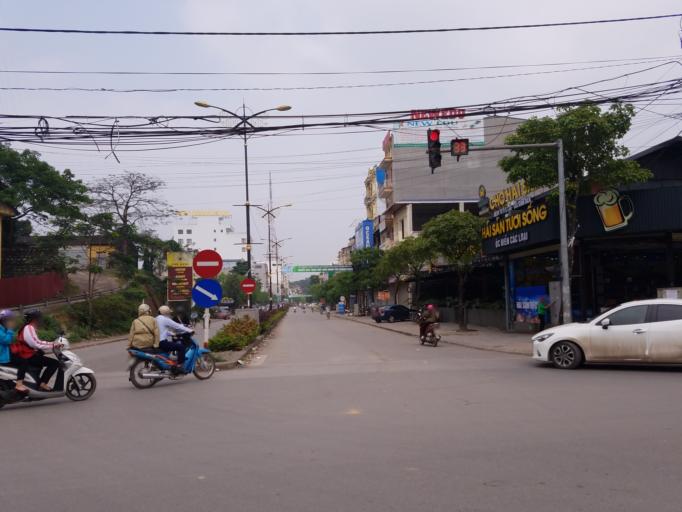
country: VN
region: Thai Nguyen
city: Thanh Pho Thai Nguyen
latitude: 21.5936
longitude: 105.8251
